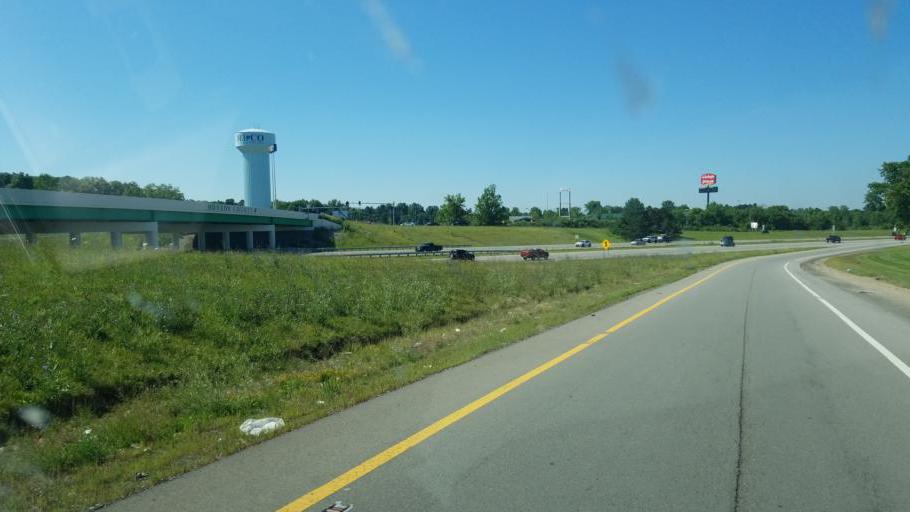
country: US
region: Ohio
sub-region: Delaware County
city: Ashley
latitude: 40.3749
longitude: -82.8298
